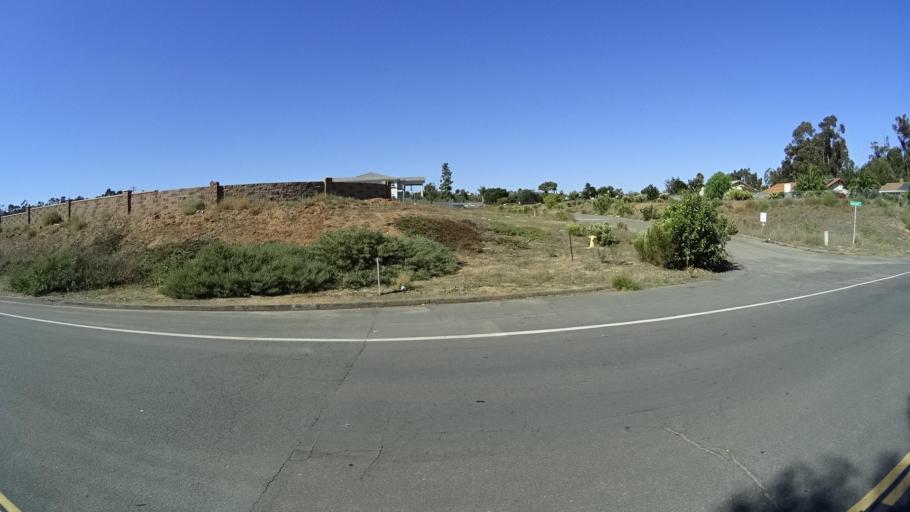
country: US
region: California
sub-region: San Diego County
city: Bonita
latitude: 32.6668
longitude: -117.0302
